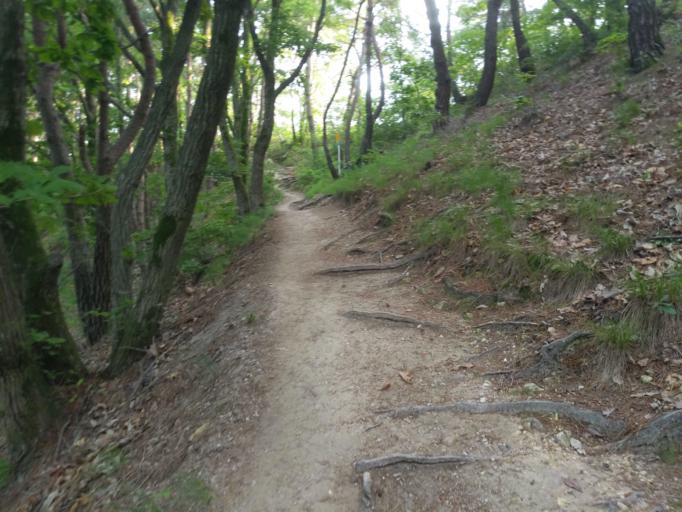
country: KR
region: Daegu
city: Hwawon
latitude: 35.7851
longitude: 128.5465
